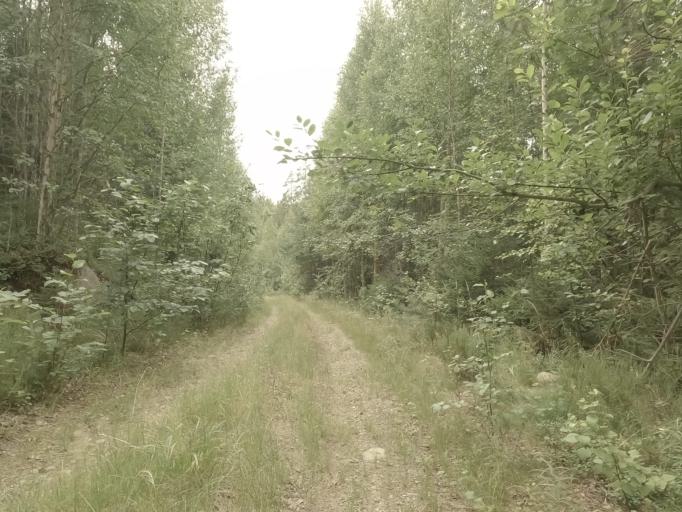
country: RU
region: Leningrad
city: Kamennogorsk
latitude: 61.0198
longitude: 29.1632
